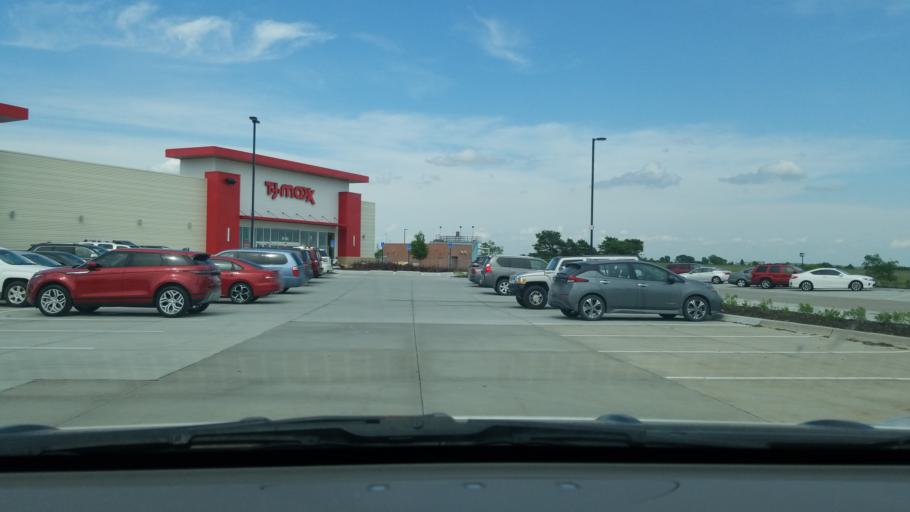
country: US
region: Nebraska
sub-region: Sarpy County
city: Gretna
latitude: 41.0990
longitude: -96.2467
